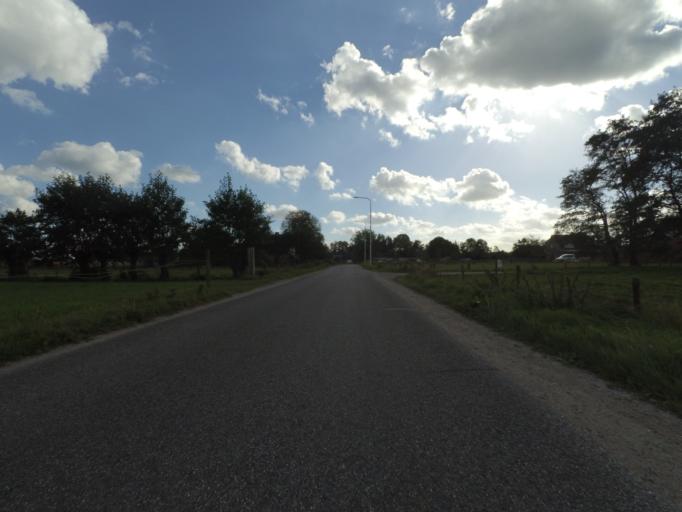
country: NL
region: Gelderland
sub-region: Gemeente Ede
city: Ederveen
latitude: 52.0519
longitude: 5.5962
